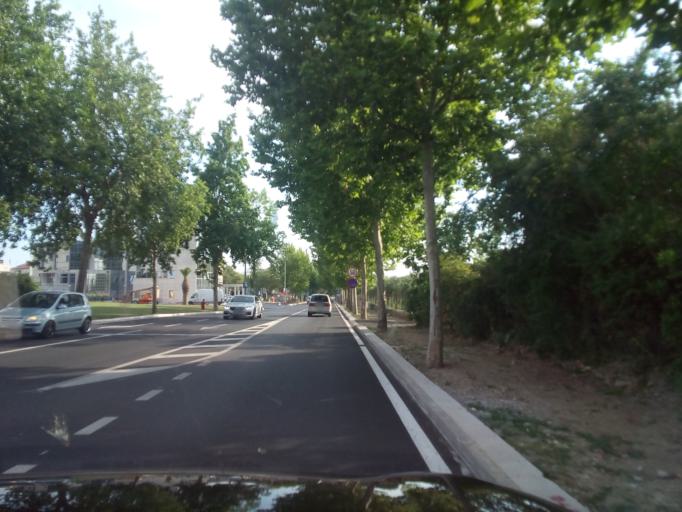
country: HR
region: Splitsko-Dalmatinska
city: Solin
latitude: 43.5389
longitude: 16.4895
